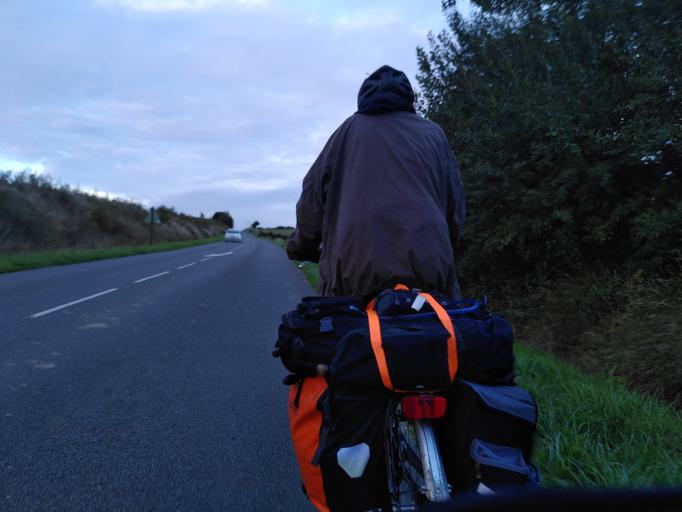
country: FR
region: Nord-Pas-de-Calais
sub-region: Departement du Pas-de-Calais
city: Therouanne
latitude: 50.6421
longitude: 2.2623
